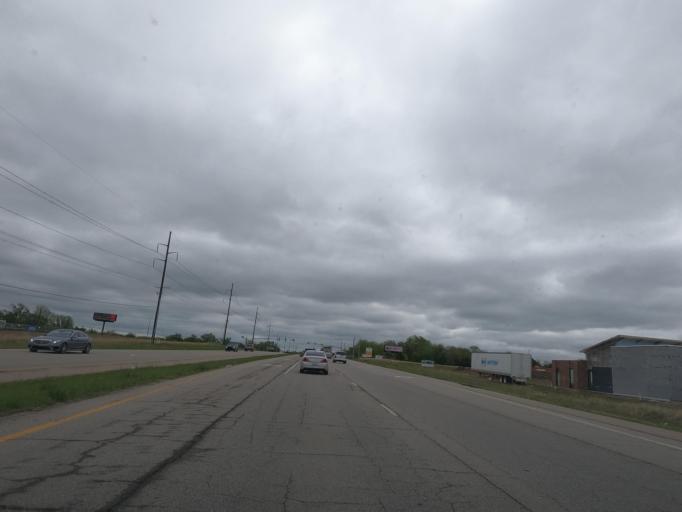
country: US
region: Kansas
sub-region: Butler County
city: Andover
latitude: 37.6796
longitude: -97.1288
